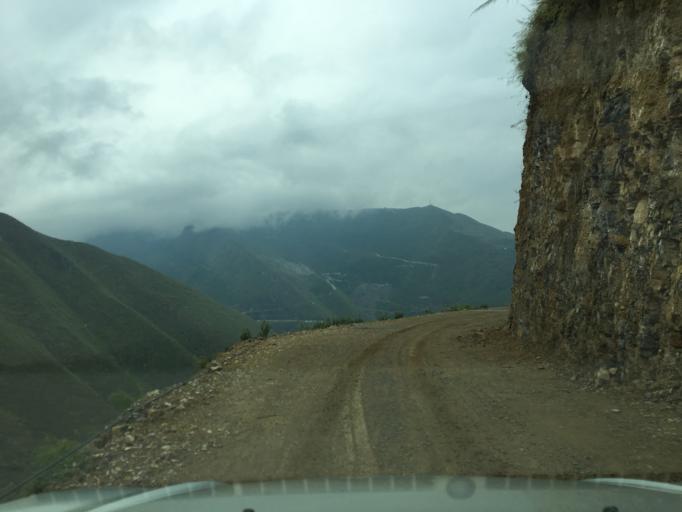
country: CN
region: Guizhou Sheng
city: Liupanshui
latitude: 25.9632
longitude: 105.2361
